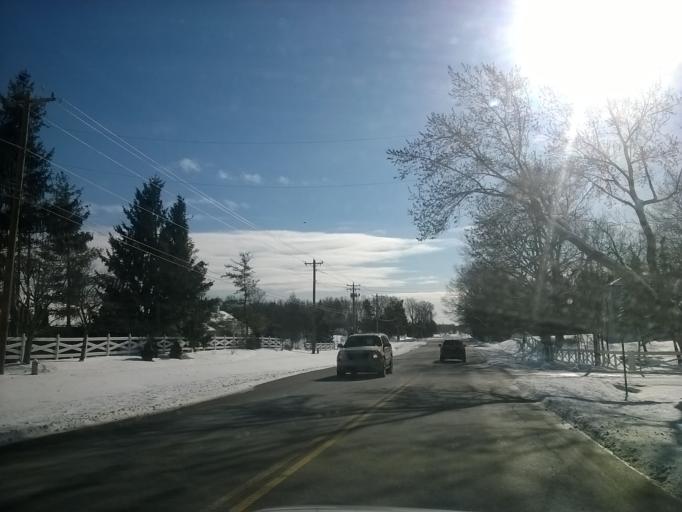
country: US
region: Indiana
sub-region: Hamilton County
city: Carmel
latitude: 39.9371
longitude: -86.1269
